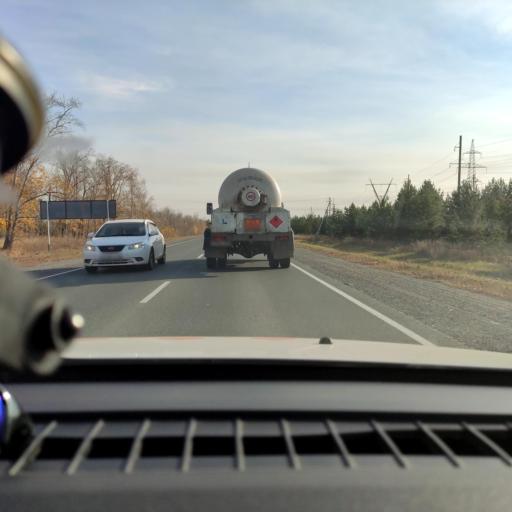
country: RU
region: Samara
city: Volzhskiy
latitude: 53.4521
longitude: 50.1337
